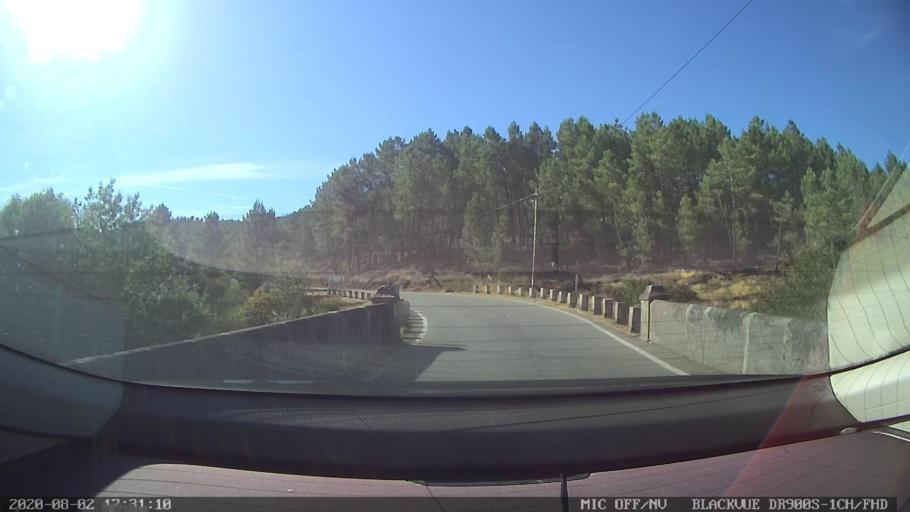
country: PT
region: Vila Real
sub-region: Sabrosa
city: Sabrosa
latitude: 41.3559
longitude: -7.5767
